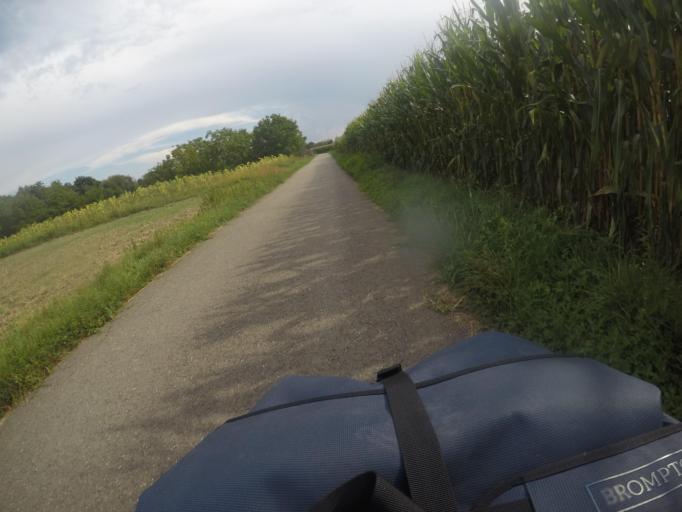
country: DE
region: Baden-Wuerttemberg
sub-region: Freiburg Region
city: Efringen-Kirchen
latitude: 47.6291
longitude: 7.5741
